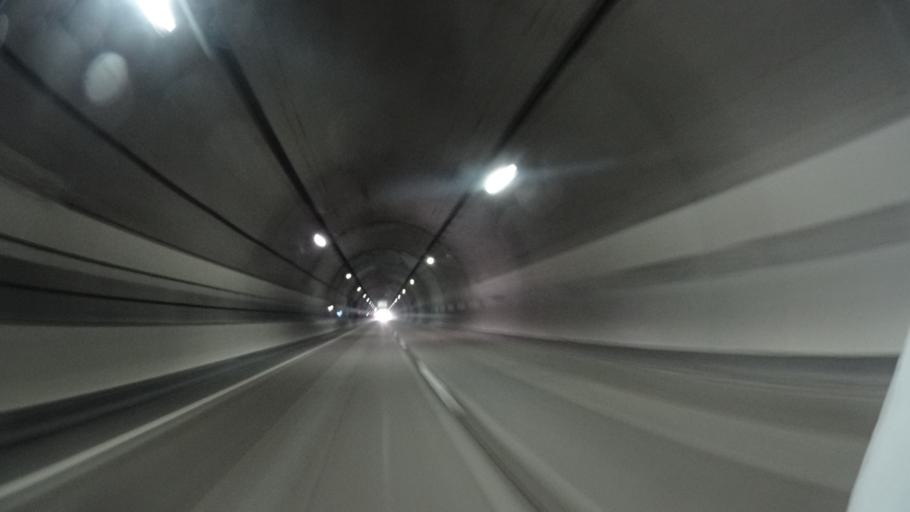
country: JP
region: Kyoto
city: Kyoto
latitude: 34.9721
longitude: 135.7881
